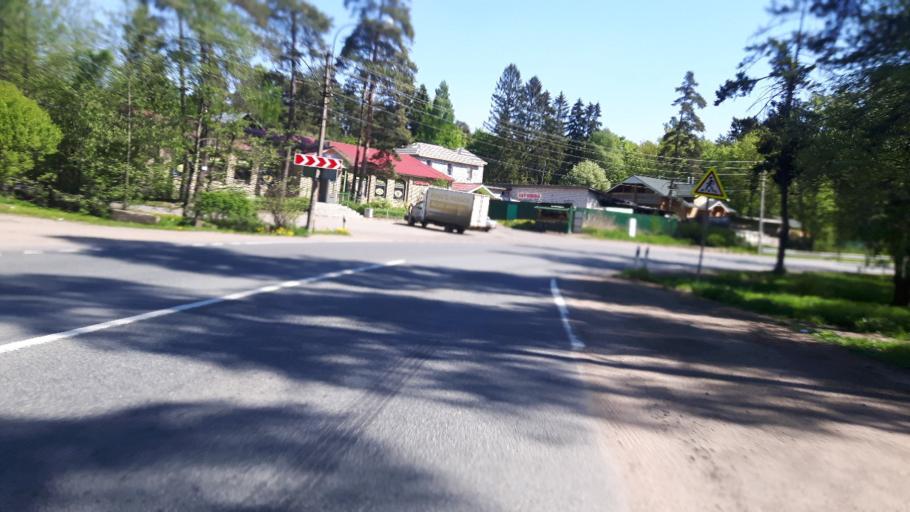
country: RU
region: St.-Petersburg
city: Zelenogorsk
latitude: 60.1938
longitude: 29.6672
